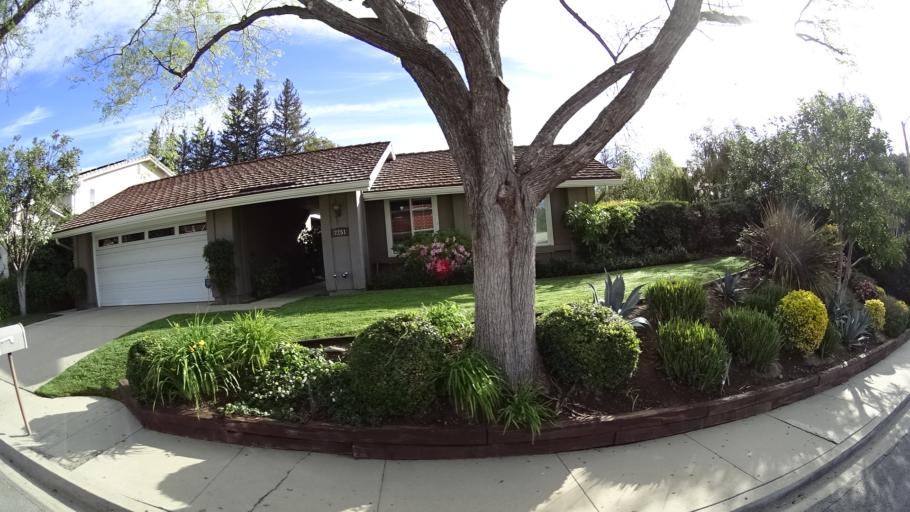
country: US
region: California
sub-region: Ventura County
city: Thousand Oaks
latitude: 34.1562
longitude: -118.8363
